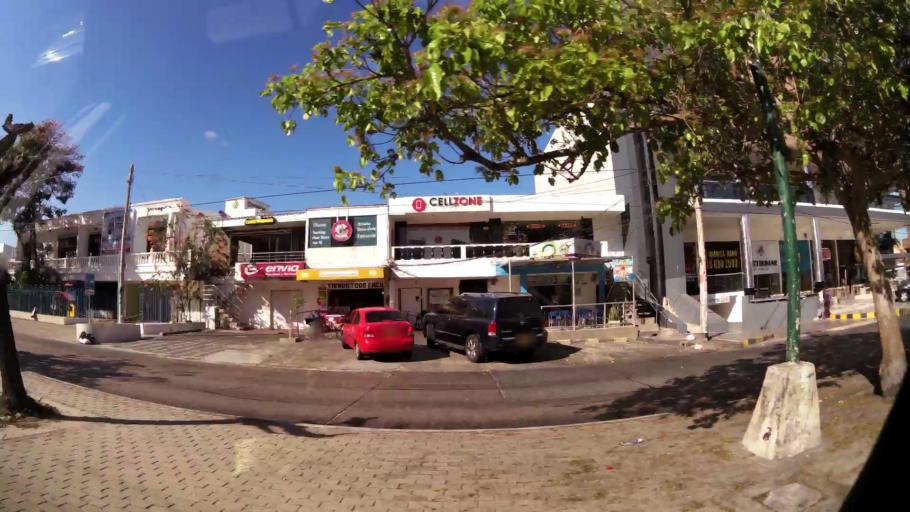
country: CO
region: Atlantico
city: Barranquilla
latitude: 11.0023
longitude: -74.8216
